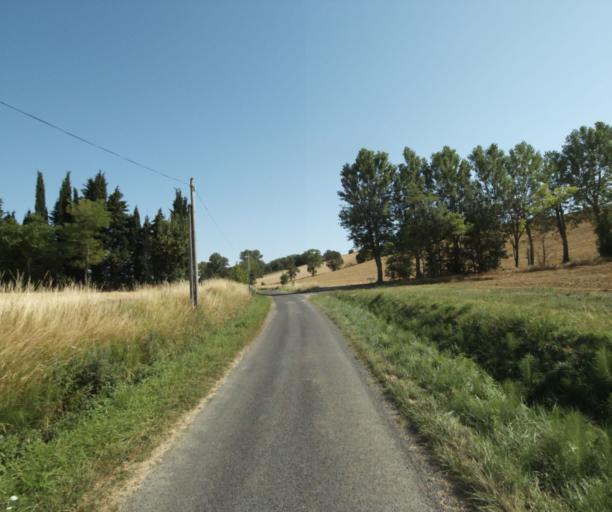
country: FR
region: Midi-Pyrenees
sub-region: Departement de la Haute-Garonne
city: Saint-Felix-Lauragais
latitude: 43.4340
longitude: 1.8463
